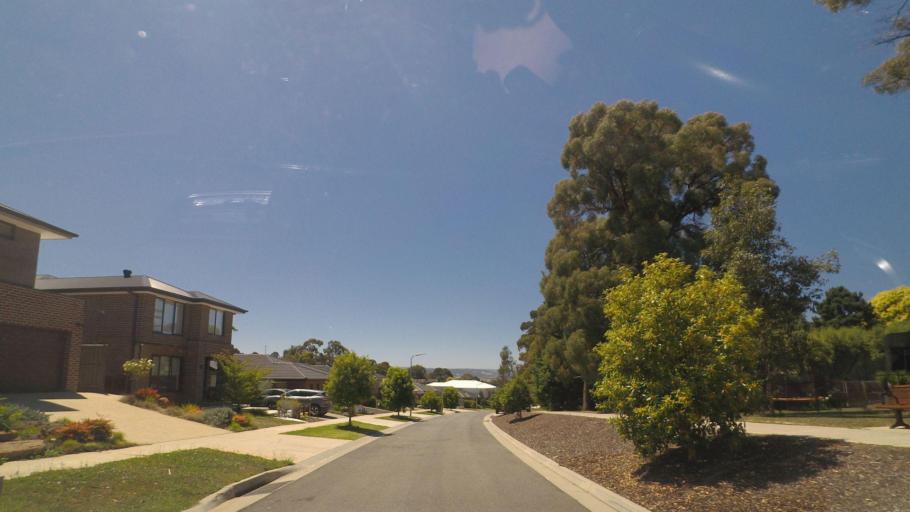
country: AU
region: Victoria
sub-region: Yarra Ranges
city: Lilydale
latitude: -37.7546
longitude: 145.3298
